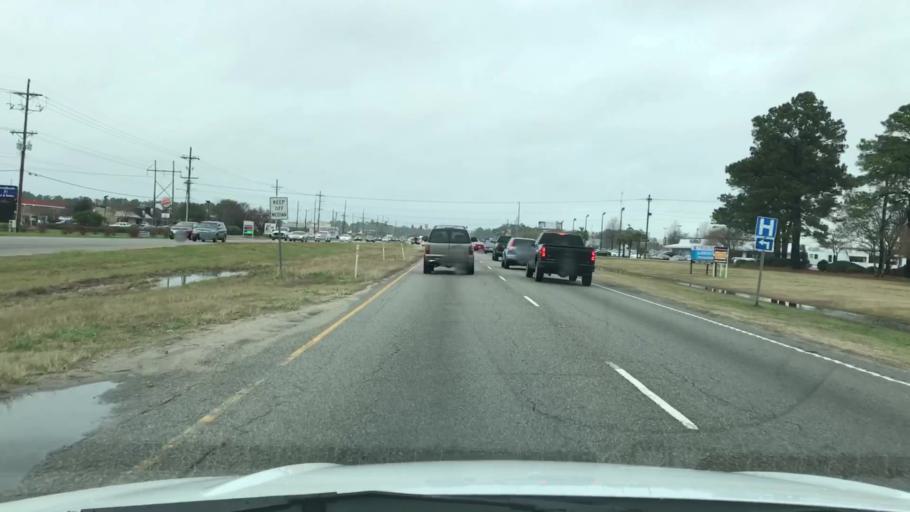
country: US
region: South Carolina
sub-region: Horry County
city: Red Hill
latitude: 33.7886
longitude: -78.9949
